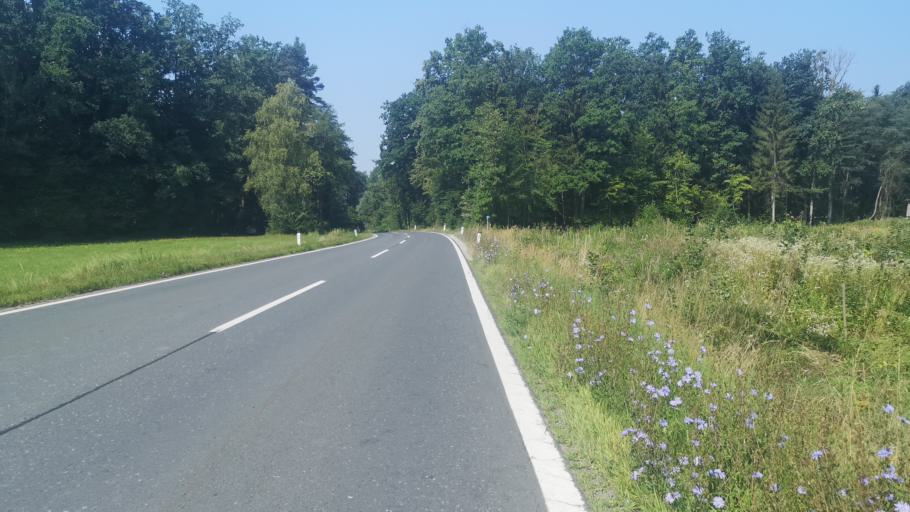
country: AT
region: Styria
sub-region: Politischer Bezirk Graz-Umgebung
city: Pirka
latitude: 46.9720
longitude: 15.3762
